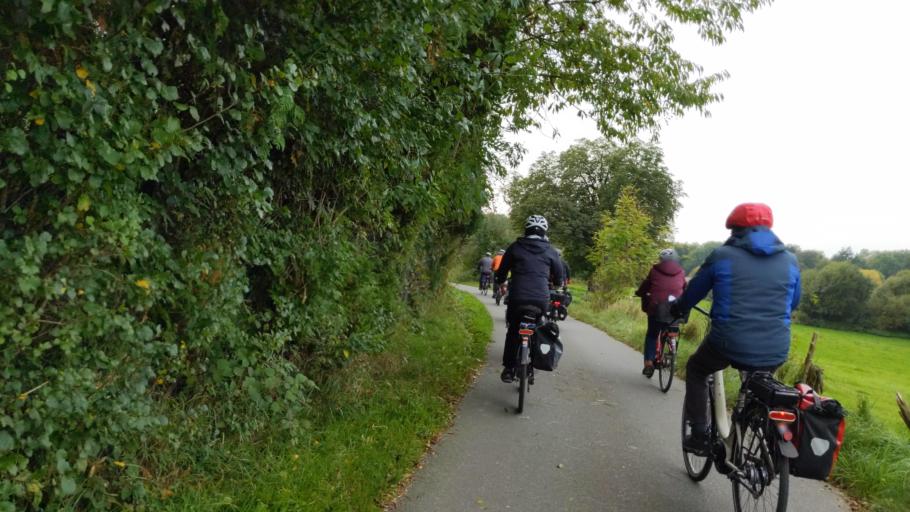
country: DE
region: Schleswig-Holstein
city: Rehhorst
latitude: 53.8589
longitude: 10.4712
